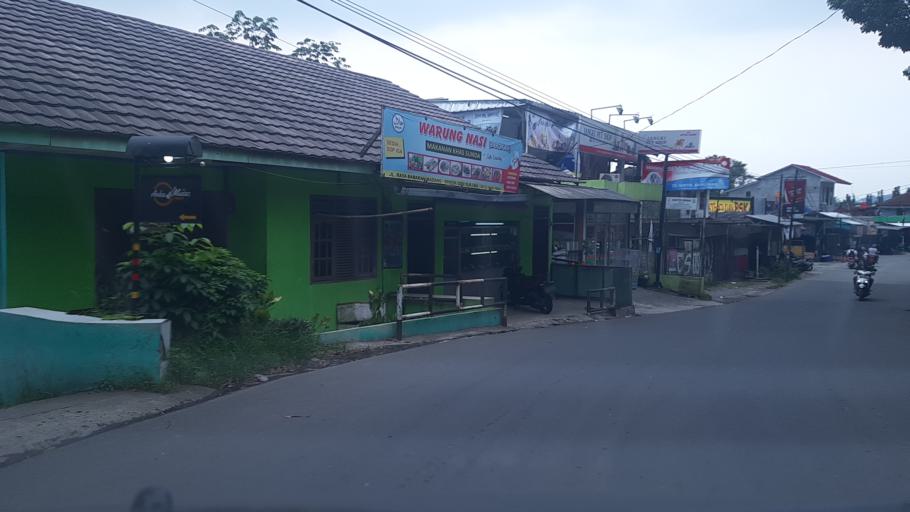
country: ID
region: West Java
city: Bogor
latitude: -6.5716
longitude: 106.8648
